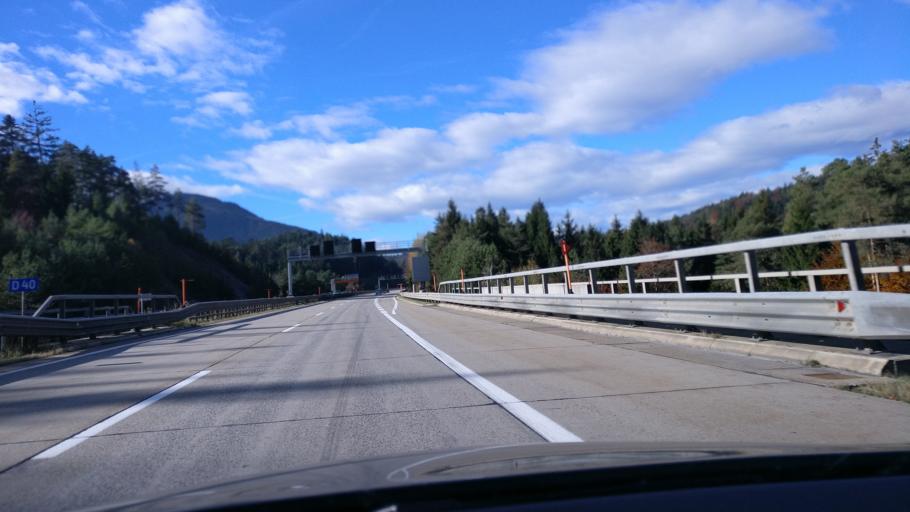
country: AT
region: Carinthia
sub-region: Politischer Bezirk Villach Land
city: Fresach
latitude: 46.6522
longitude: 13.7445
